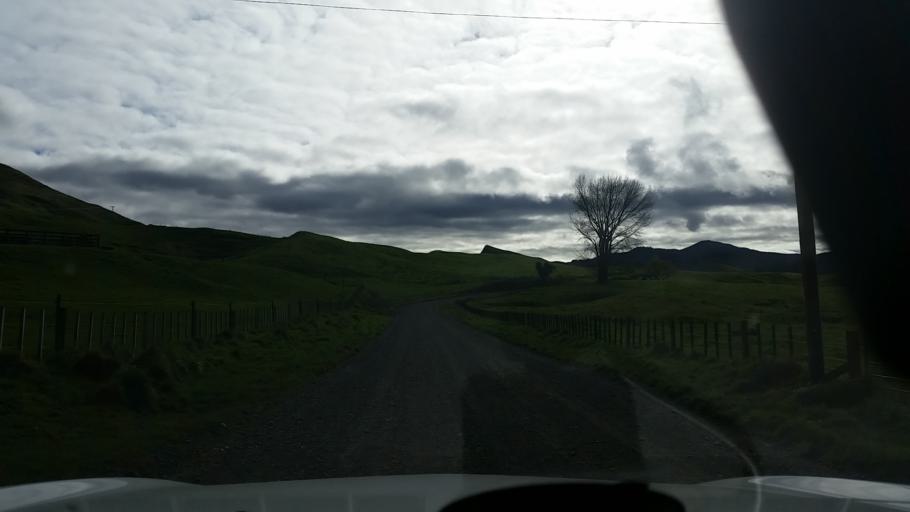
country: NZ
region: Hawke's Bay
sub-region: Napier City
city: Napier
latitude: -39.1231
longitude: 176.8952
